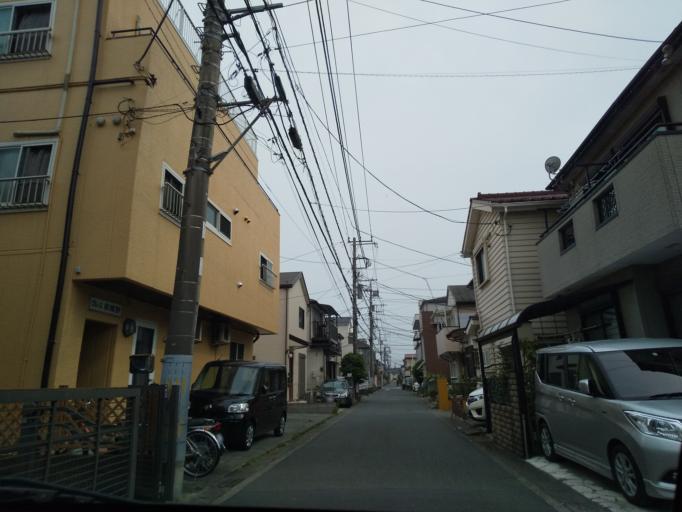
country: JP
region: Kanagawa
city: Minami-rinkan
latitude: 35.4657
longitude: 139.4259
